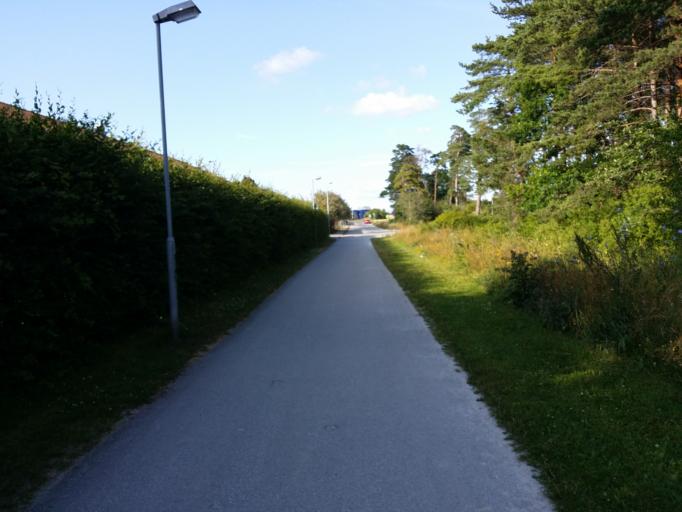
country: SE
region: Gotland
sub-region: Gotland
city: Visby
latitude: 57.6295
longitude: 18.3237
